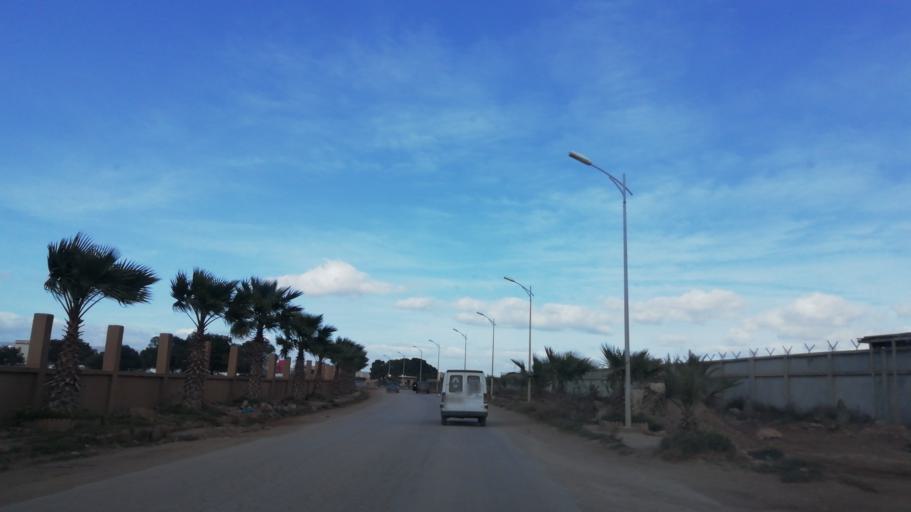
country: DZ
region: Oran
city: Es Senia
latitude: 35.6344
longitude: -0.5847
